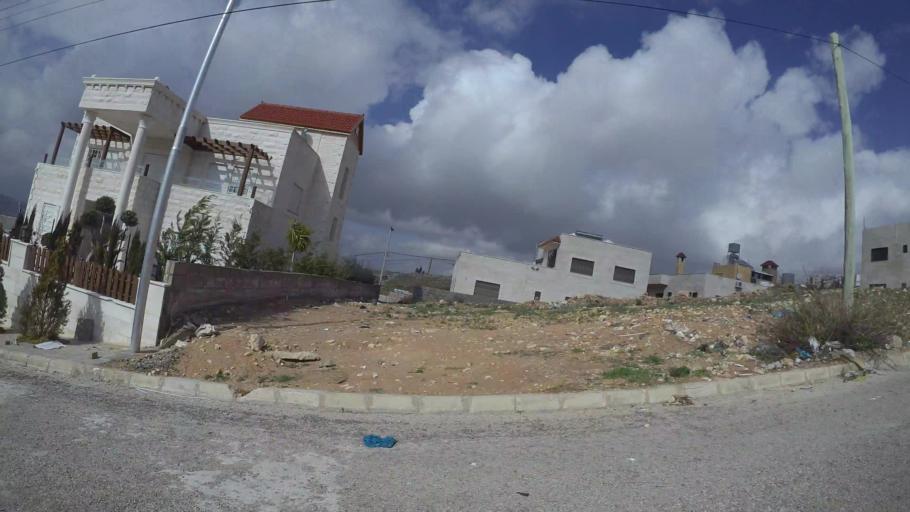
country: JO
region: Amman
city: Al Jubayhah
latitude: 32.0601
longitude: 35.8633
